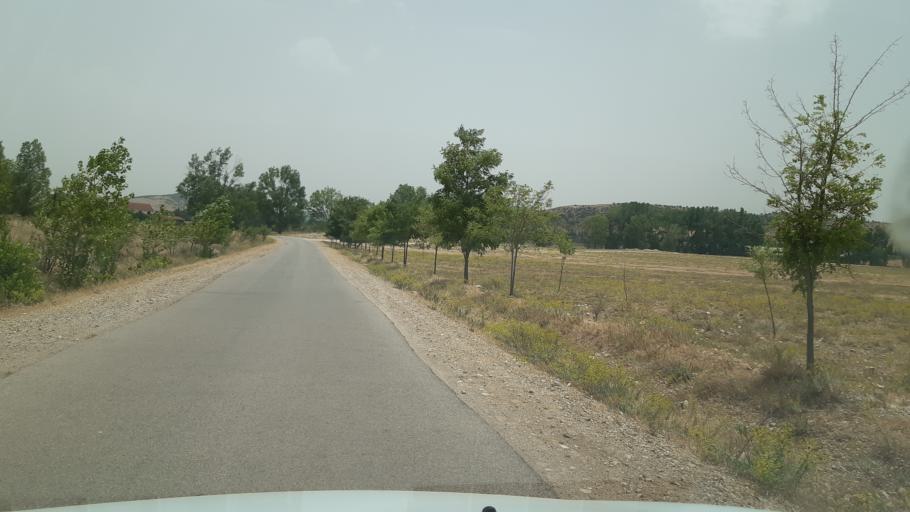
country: MA
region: Meknes-Tafilalet
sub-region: Ifrane
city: Ifrane
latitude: 33.6475
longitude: -5.0218
